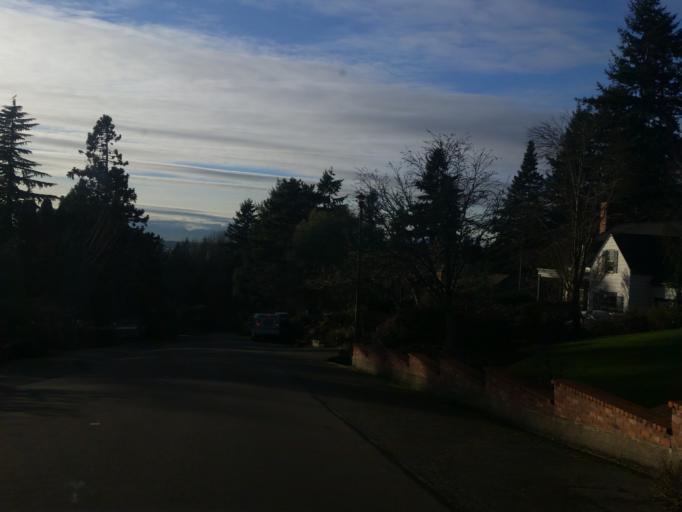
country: US
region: Washington
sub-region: King County
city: Shoreline
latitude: 47.7131
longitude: -122.3656
